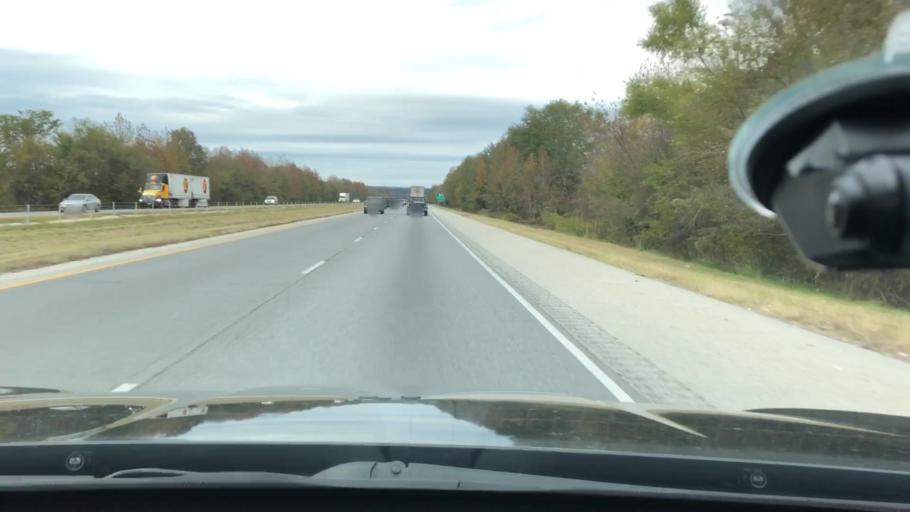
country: US
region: Arkansas
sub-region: Clark County
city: Arkadelphia
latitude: 34.1641
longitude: -93.0761
